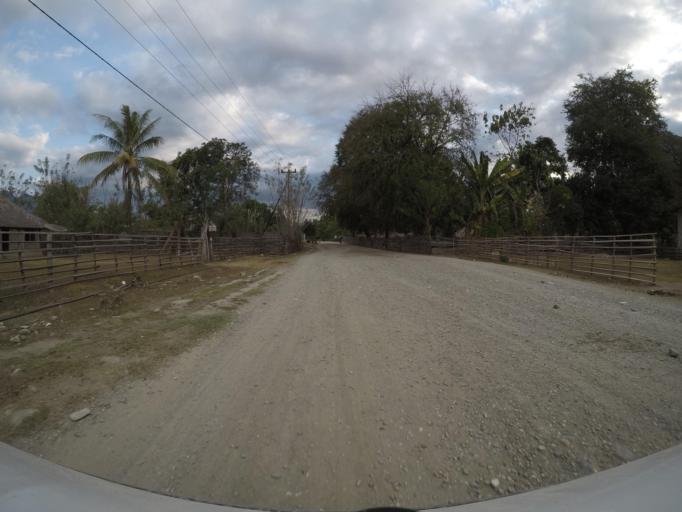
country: TL
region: Bobonaro
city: Maliana
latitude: -8.8714
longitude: 125.2126
